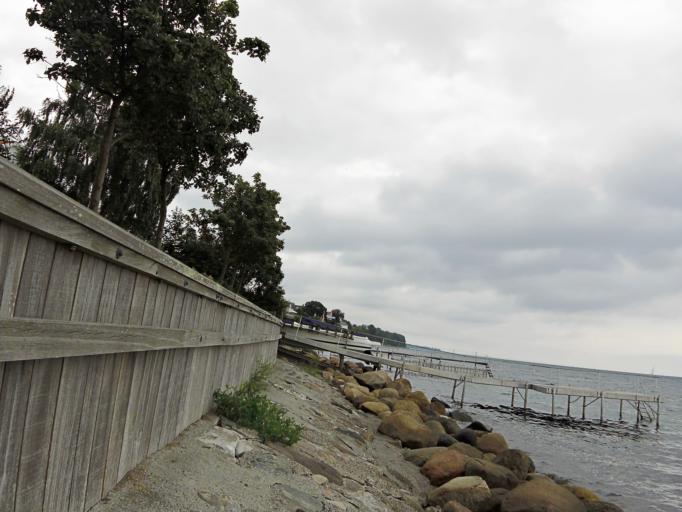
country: DK
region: Capital Region
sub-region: Gentofte Kommune
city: Charlottenlund
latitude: 55.7904
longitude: 12.5939
